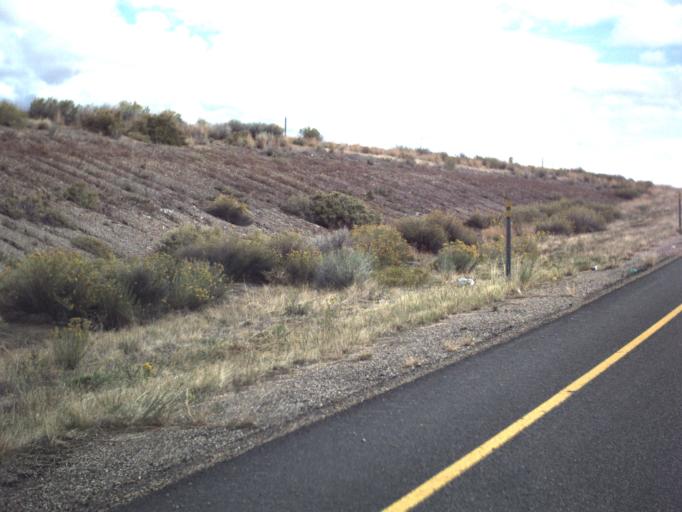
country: US
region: Utah
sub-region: Grand County
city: Moab
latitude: 38.9420
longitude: -109.8148
